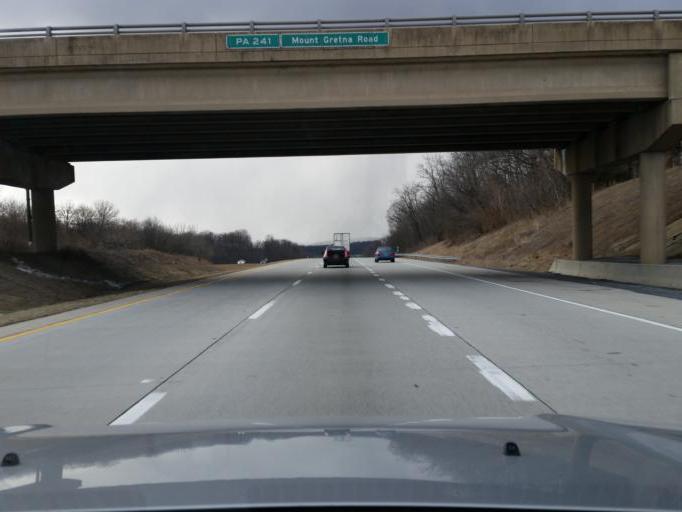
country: US
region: Pennsylvania
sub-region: Lancaster County
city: Elizabethtown
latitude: 40.1741
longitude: -76.5955
